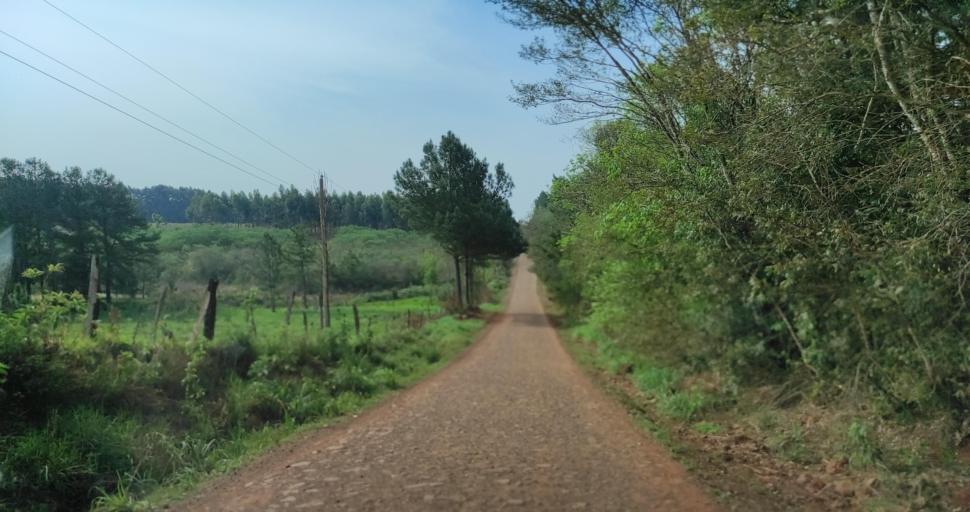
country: AR
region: Misiones
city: Garuhape
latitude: -26.8720
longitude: -55.0056
